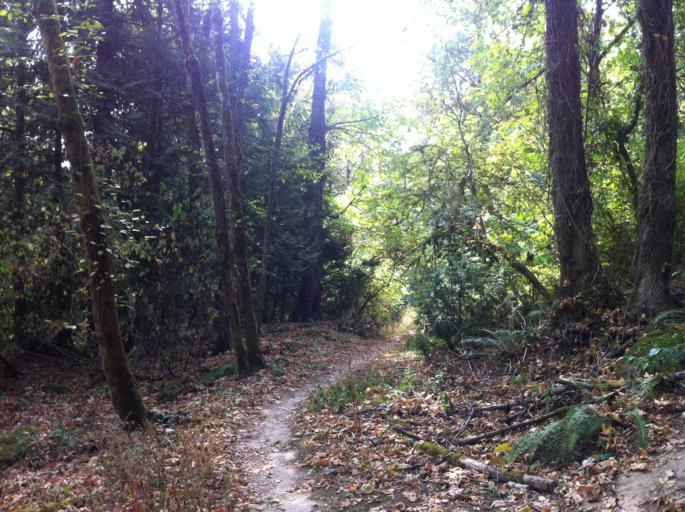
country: US
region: Oregon
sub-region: Clackamas County
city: Lake Oswego
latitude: 45.4542
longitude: -122.6742
